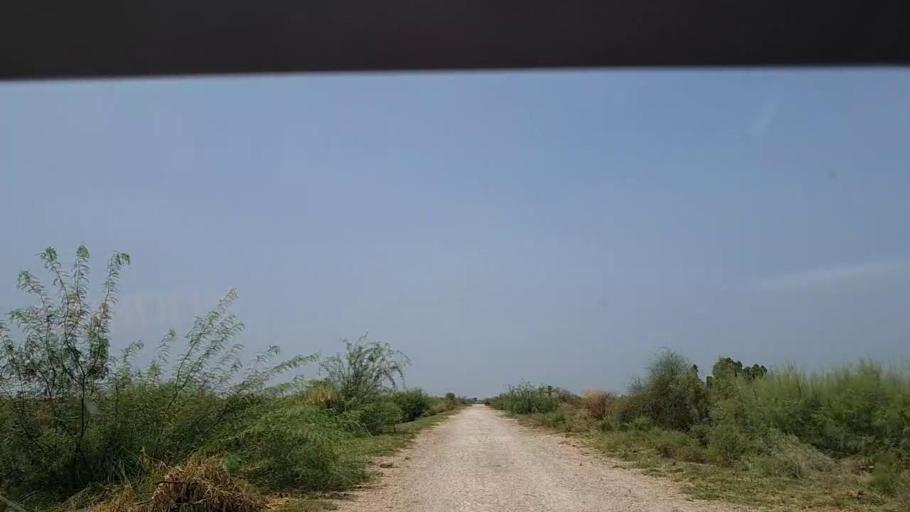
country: PK
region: Sindh
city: Adilpur
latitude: 27.8940
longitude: 69.2446
